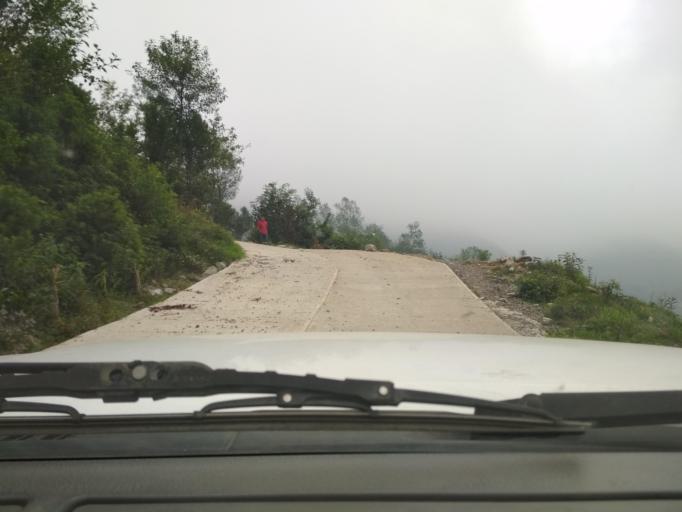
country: MX
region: Veracruz
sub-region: La Perla
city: Metlac Hernandez (Metlac Primero)
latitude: 18.9619
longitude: -97.1462
